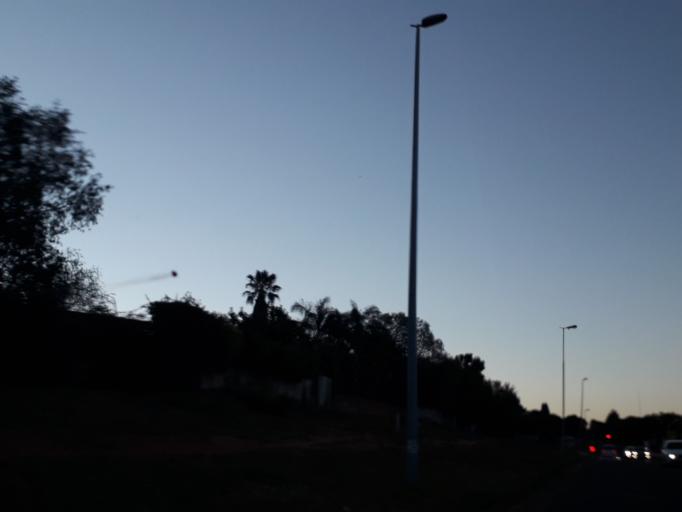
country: ZA
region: Gauteng
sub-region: City of Johannesburg Metropolitan Municipality
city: Roodepoort
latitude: -26.1140
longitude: 27.9325
